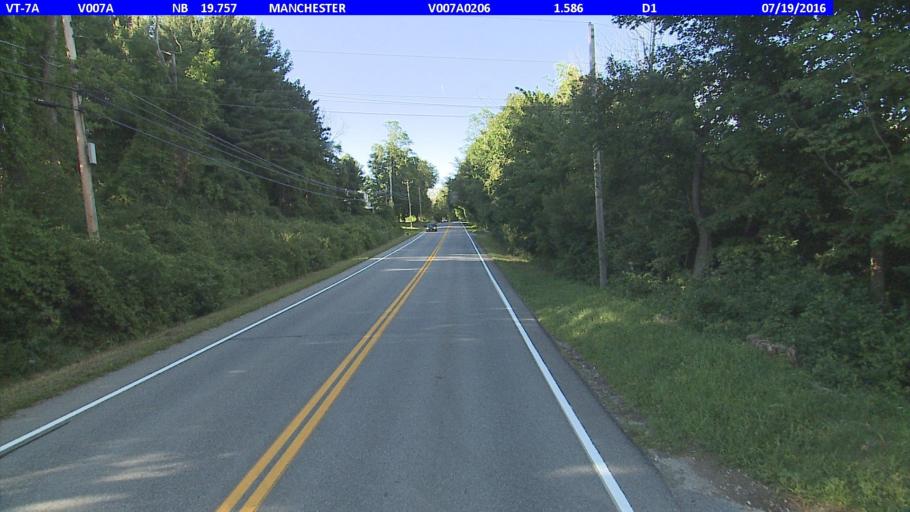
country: US
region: Vermont
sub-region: Bennington County
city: Manchester Center
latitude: 43.1396
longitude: -73.0916
